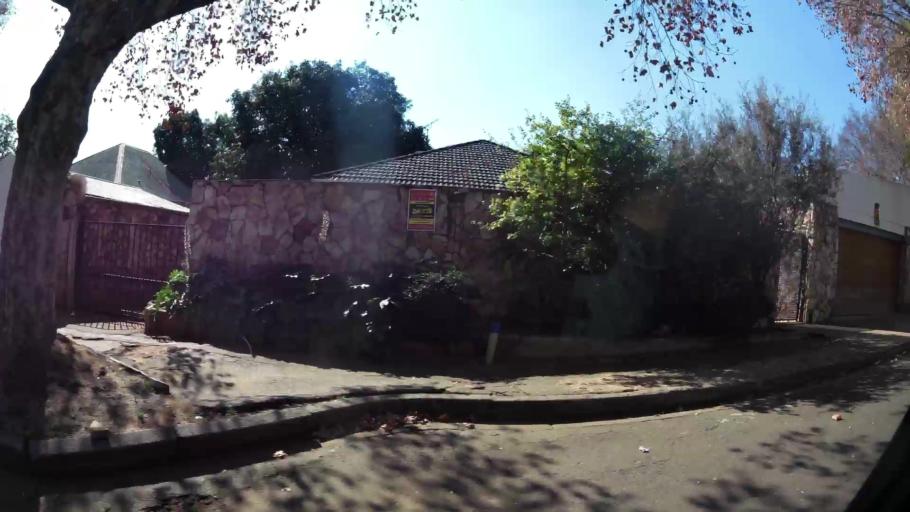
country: ZA
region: Gauteng
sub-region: City of Johannesburg Metropolitan Municipality
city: Johannesburg
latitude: -26.1645
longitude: 28.0299
